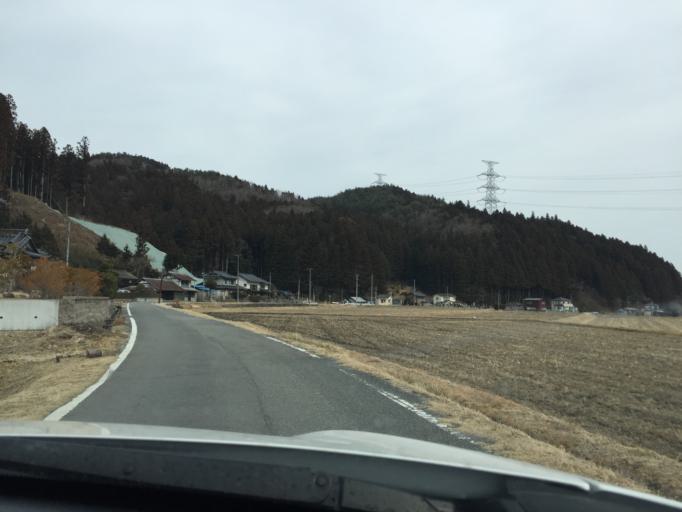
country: JP
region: Fukushima
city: Iwaki
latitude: 37.1391
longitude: 140.6966
